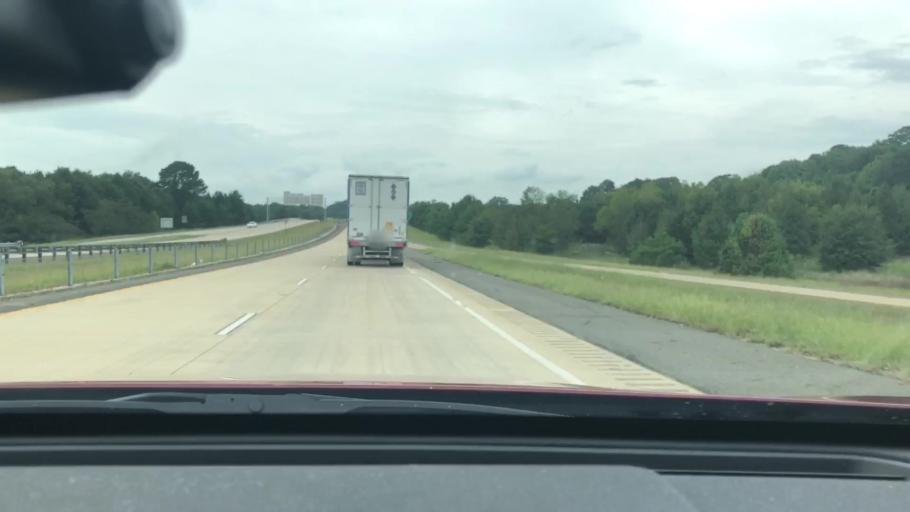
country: US
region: Texas
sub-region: Bowie County
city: Texarkana
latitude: 33.3869
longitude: -94.0224
